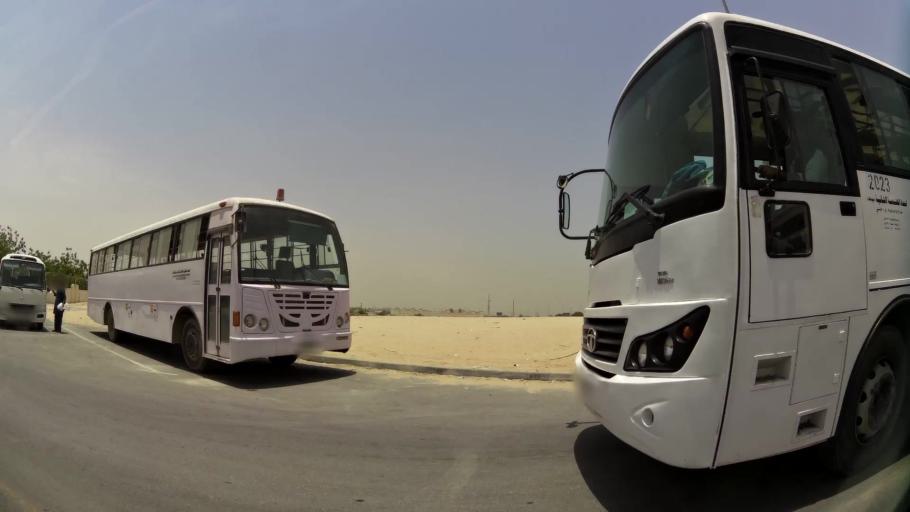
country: AE
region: Ash Shariqah
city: Sharjah
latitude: 25.2744
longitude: 55.4215
